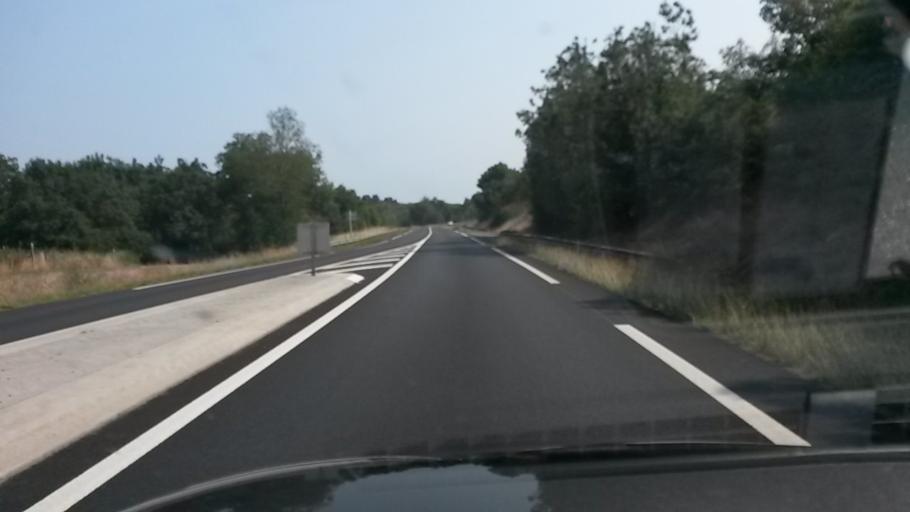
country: FR
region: Pays de la Loire
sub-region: Departement de la Loire-Atlantique
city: Ancenis
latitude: 47.3767
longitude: -1.1701
